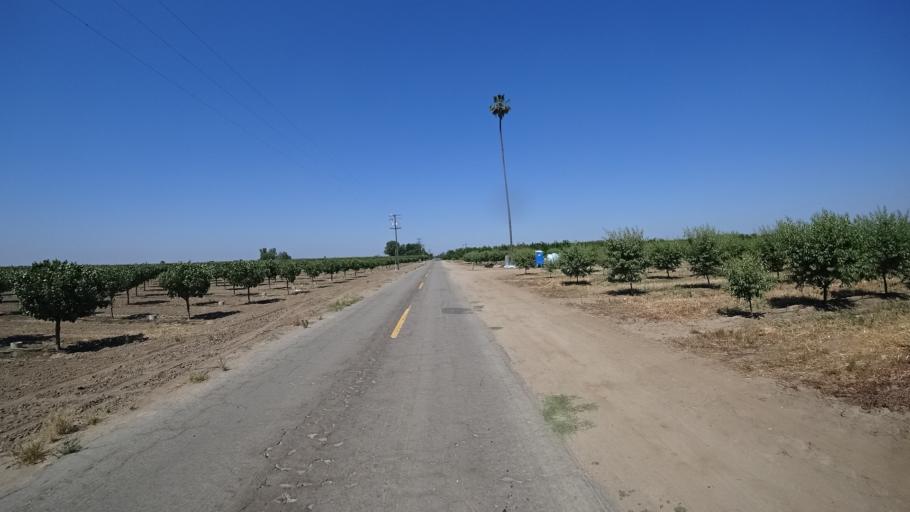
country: US
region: California
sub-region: Fresno County
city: Kingsburg
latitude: 36.4741
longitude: -119.5562
